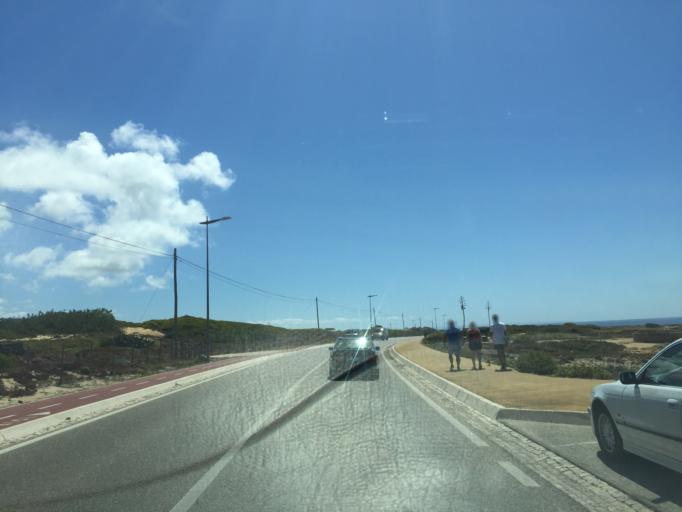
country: PT
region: Lisbon
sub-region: Cascais
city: Cascais
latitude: 38.7054
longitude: -9.4798
